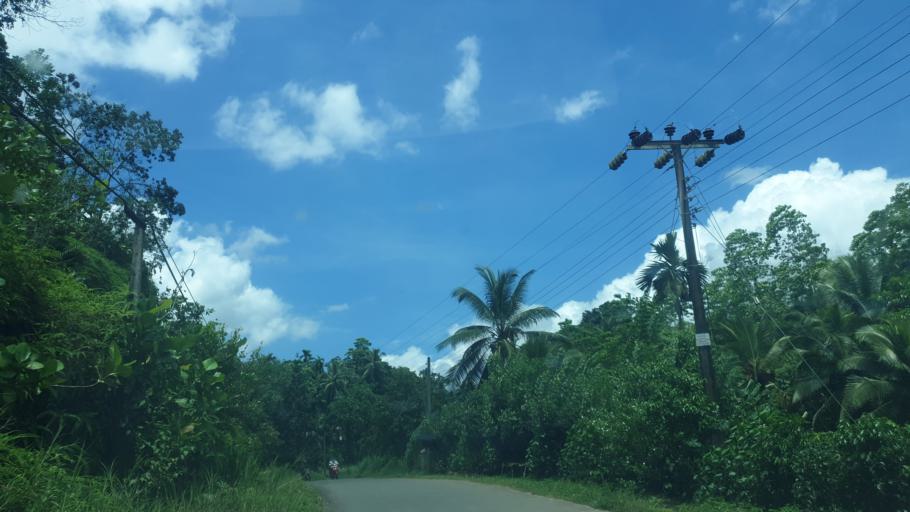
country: LK
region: Sabaragamuwa
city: Ratnapura
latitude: 6.4746
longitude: 80.4194
